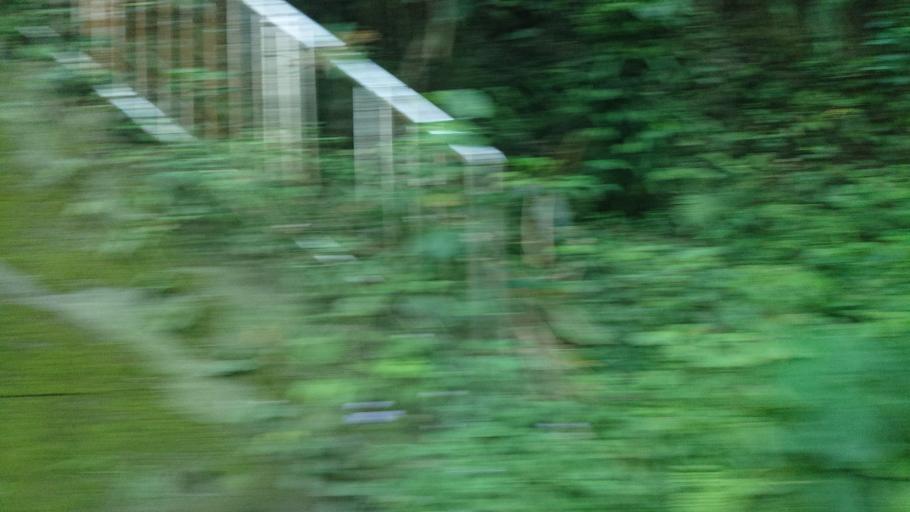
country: TW
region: Taiwan
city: Daxi
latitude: 24.8786
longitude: 121.3810
